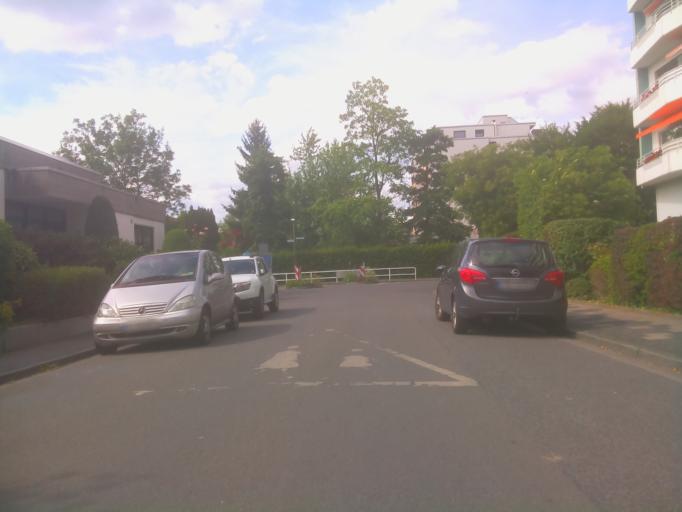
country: DE
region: Baden-Wuerttemberg
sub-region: Karlsruhe Region
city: Dossenheim
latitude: 49.4333
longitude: 8.6790
